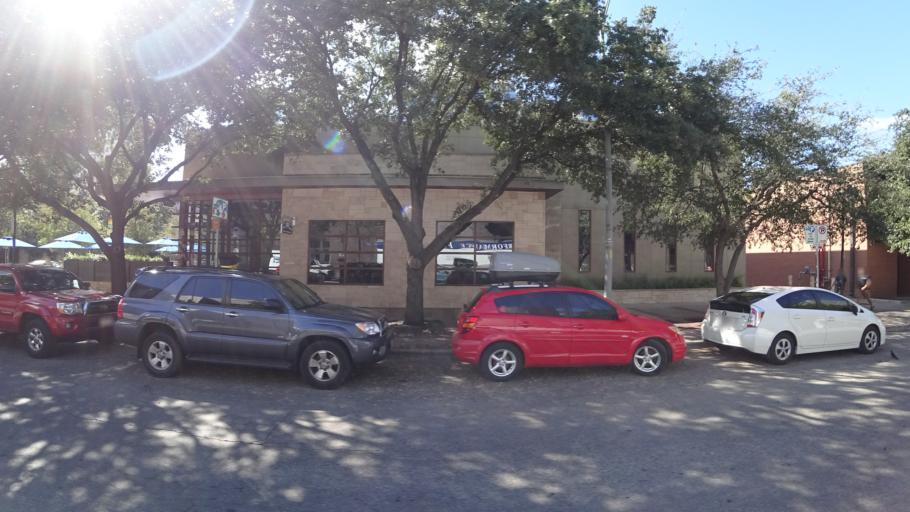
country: US
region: Texas
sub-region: Travis County
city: Austin
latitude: 30.2636
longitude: -97.7406
